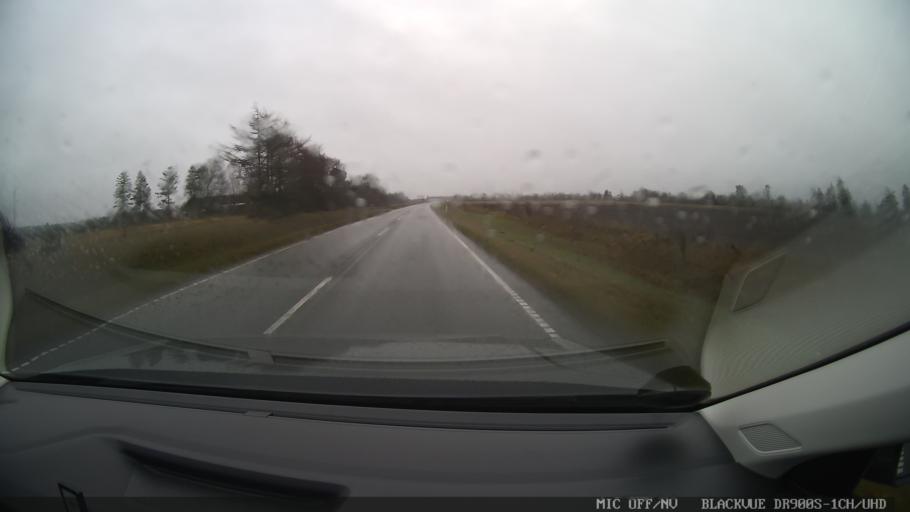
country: DK
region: Central Jutland
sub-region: Herning Kommune
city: Sunds
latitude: 56.2857
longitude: 8.9313
